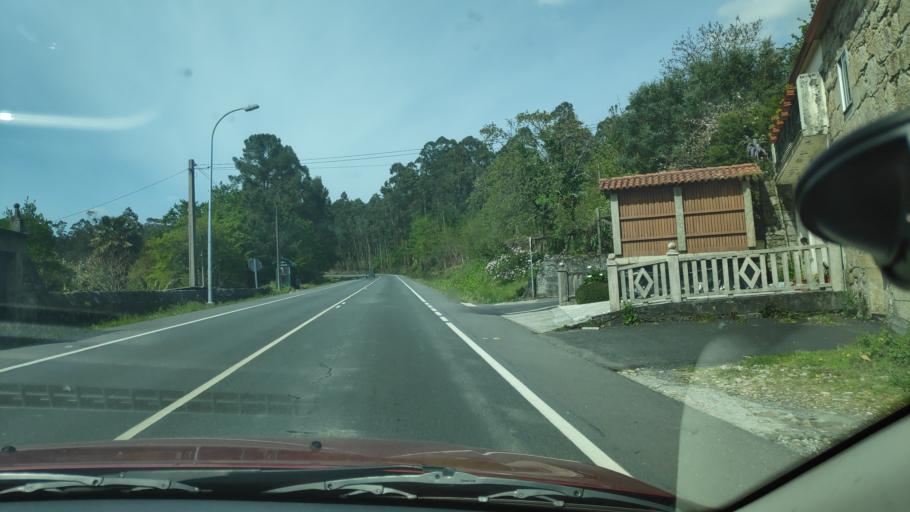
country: ES
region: Galicia
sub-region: Provincia da Coruna
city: Ames
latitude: 42.8723
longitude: -8.6589
